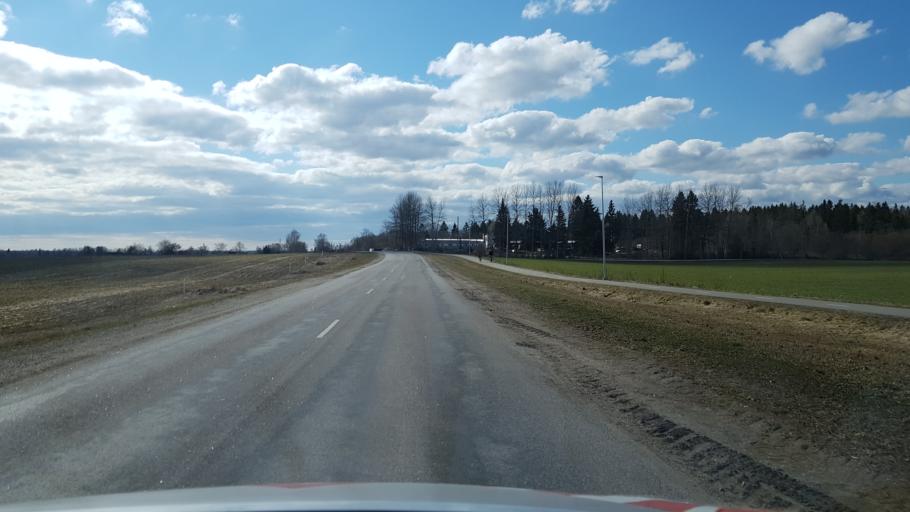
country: EE
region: Laeaene-Virumaa
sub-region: Rakvere linn
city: Rakvere
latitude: 59.3334
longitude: 26.3155
